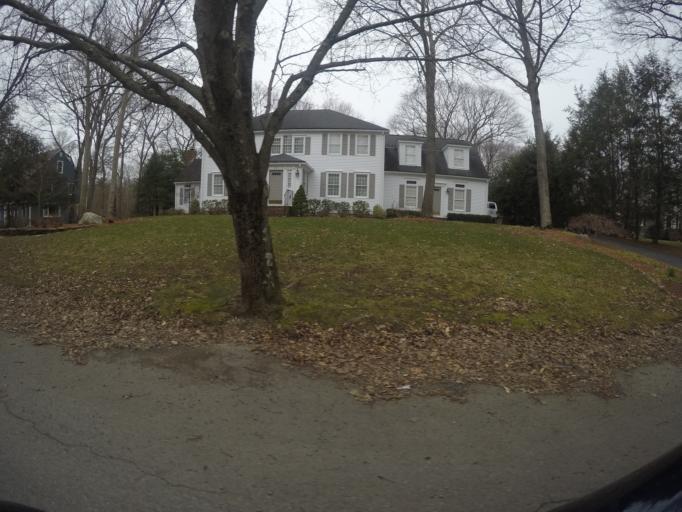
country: US
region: Massachusetts
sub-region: Bristol County
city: Easton
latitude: 42.0544
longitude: -71.1447
